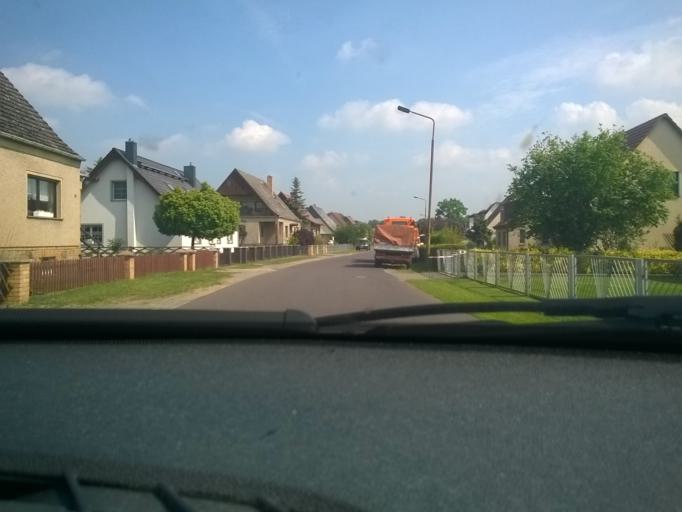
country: DE
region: Brandenburg
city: Wittstock
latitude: 53.1853
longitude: 12.4930
